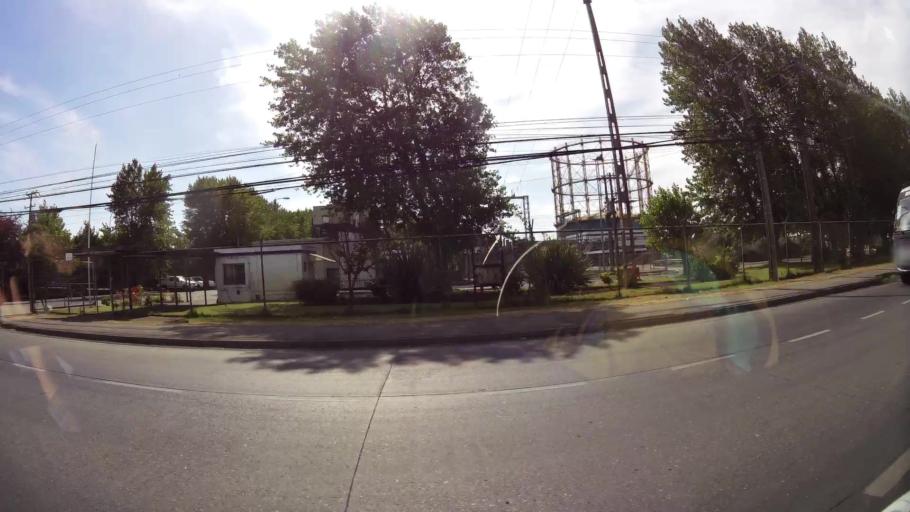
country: CL
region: Biobio
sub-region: Provincia de Concepcion
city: Talcahuano
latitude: -36.7756
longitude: -73.1132
